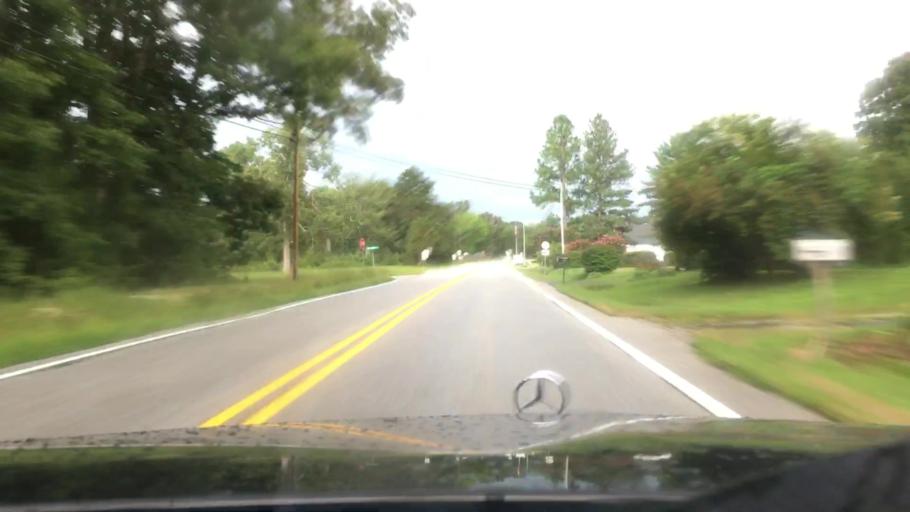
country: US
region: Virginia
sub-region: Nelson County
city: Lovingston
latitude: 37.7645
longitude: -78.9787
